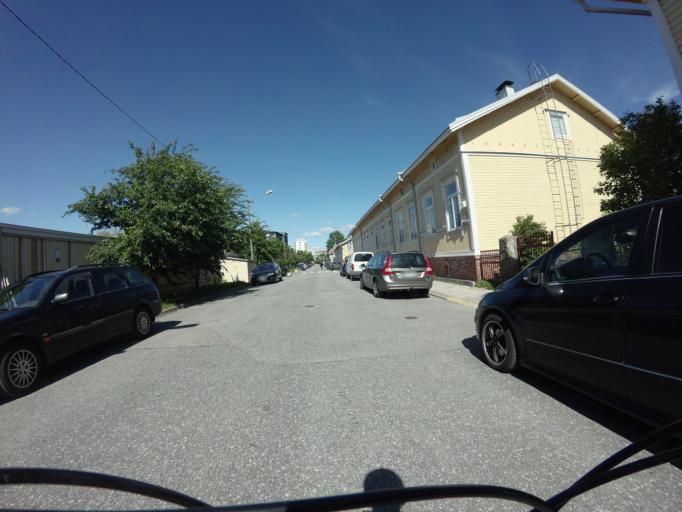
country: FI
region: Varsinais-Suomi
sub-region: Turku
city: Turku
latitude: 60.4491
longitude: 22.2431
